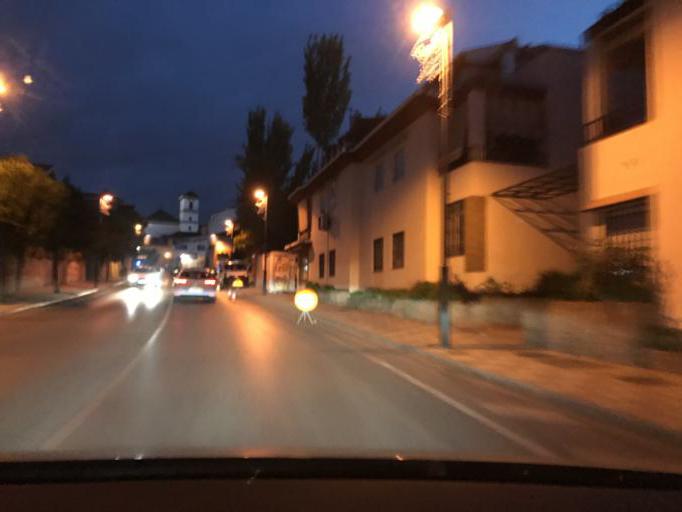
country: ES
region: Andalusia
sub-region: Provincia de Granada
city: Zubia
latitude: 37.1227
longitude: -3.5856
